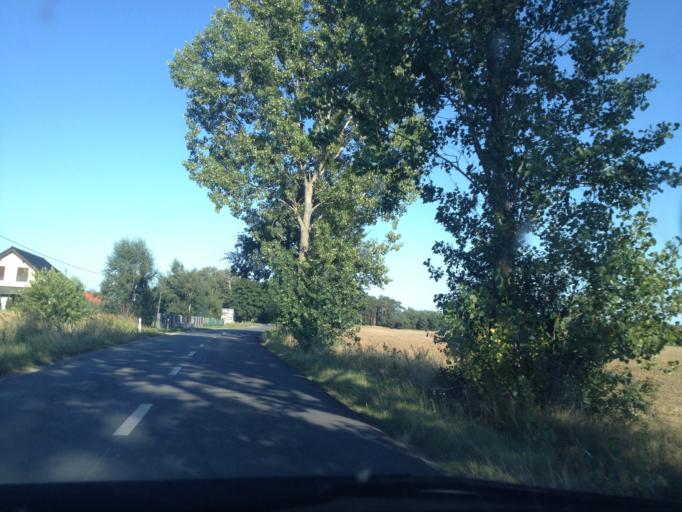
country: PL
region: Greater Poland Voivodeship
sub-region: Powiat sredzki
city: Zaniemysl
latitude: 52.1107
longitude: 17.0969
